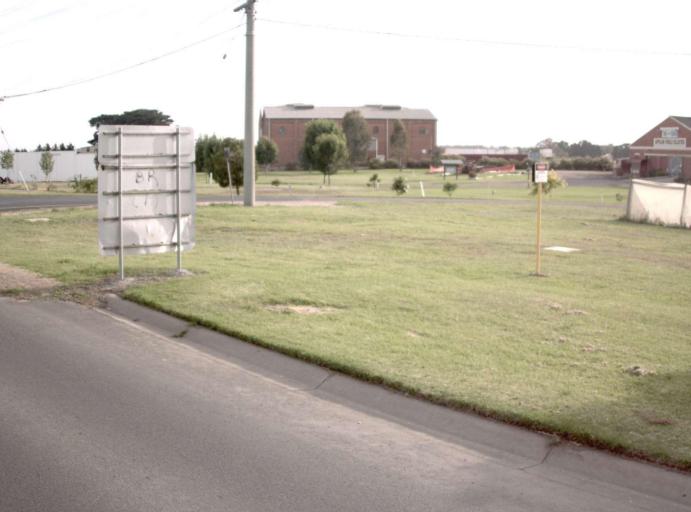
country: AU
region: Victoria
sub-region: Wellington
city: Sale
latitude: -37.9720
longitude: 146.9841
